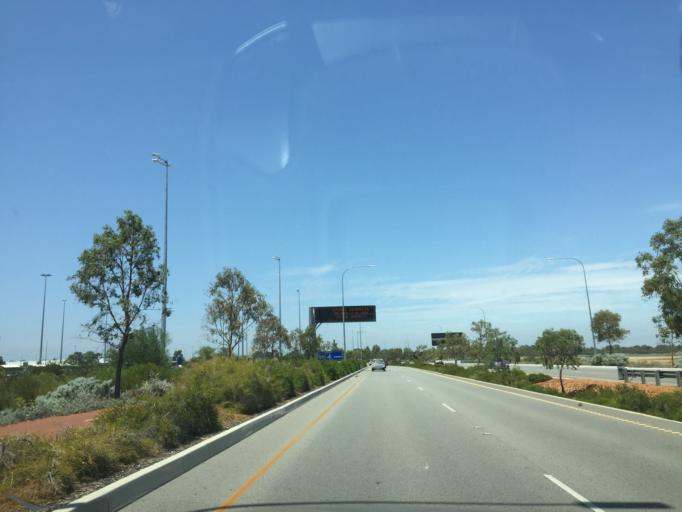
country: AU
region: Western Australia
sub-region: Belmont
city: Redcliffe
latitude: -31.9525
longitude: 115.9699
